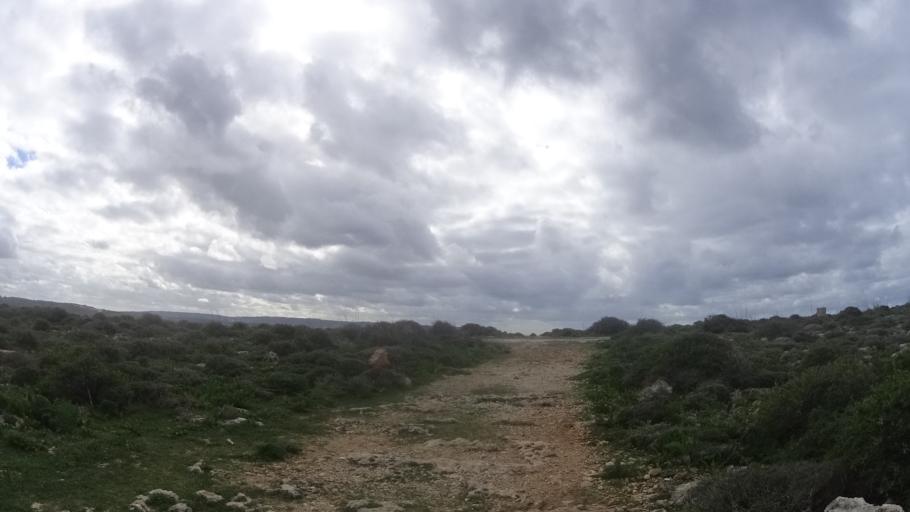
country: MT
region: Il-Mellieha
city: Mellieha
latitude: 35.9724
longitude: 14.3263
